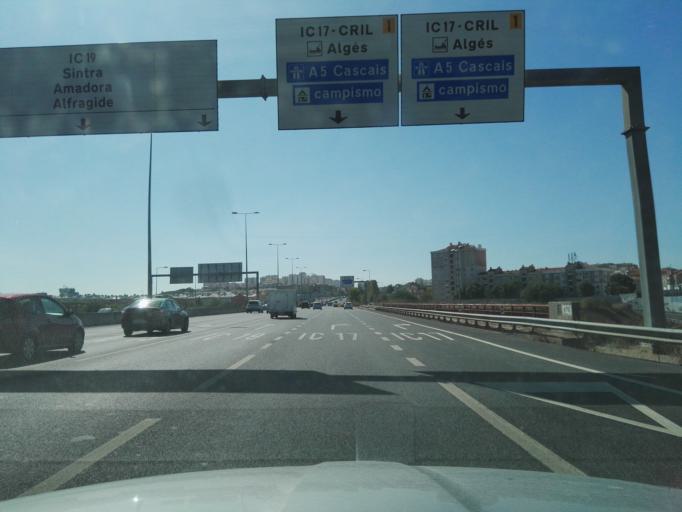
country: PT
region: Lisbon
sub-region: Odivelas
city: Pontinha
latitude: 38.7406
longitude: -9.2039
